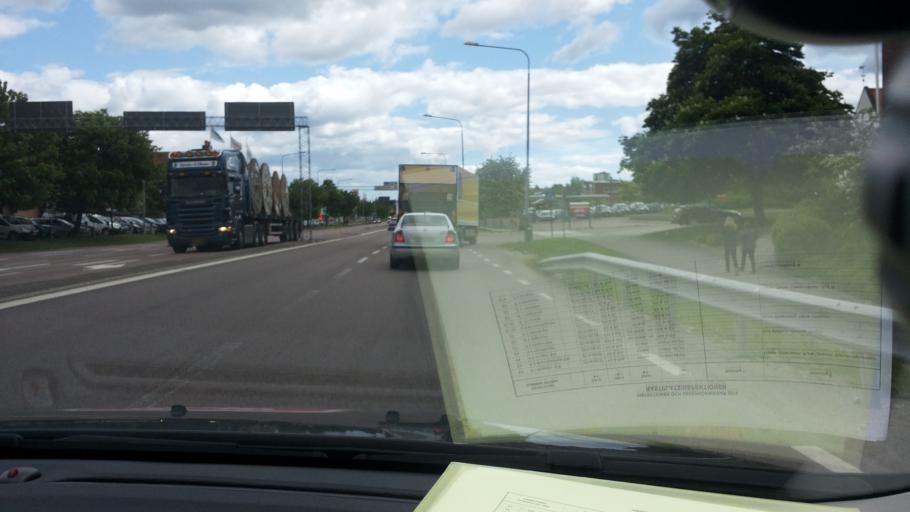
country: SE
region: Vaesternorrland
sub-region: Sundsvalls Kommun
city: Sundsvall
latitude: 62.3880
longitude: 17.3141
